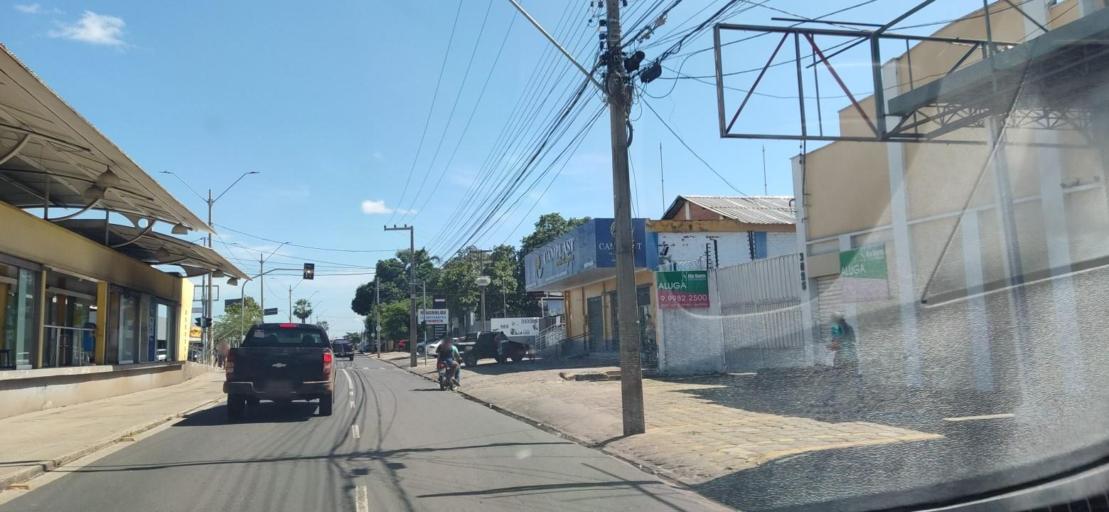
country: BR
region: Piaui
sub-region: Teresina
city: Teresina
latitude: -5.1176
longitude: -42.8038
